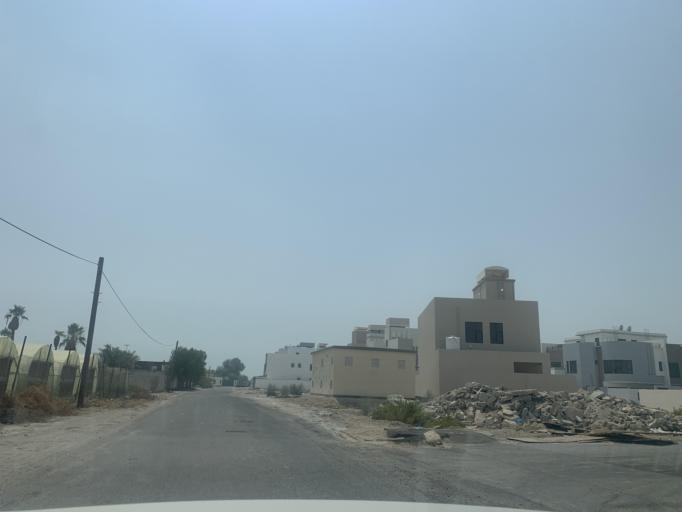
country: BH
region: Central Governorate
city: Madinat Hamad
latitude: 26.1278
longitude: 50.4700
